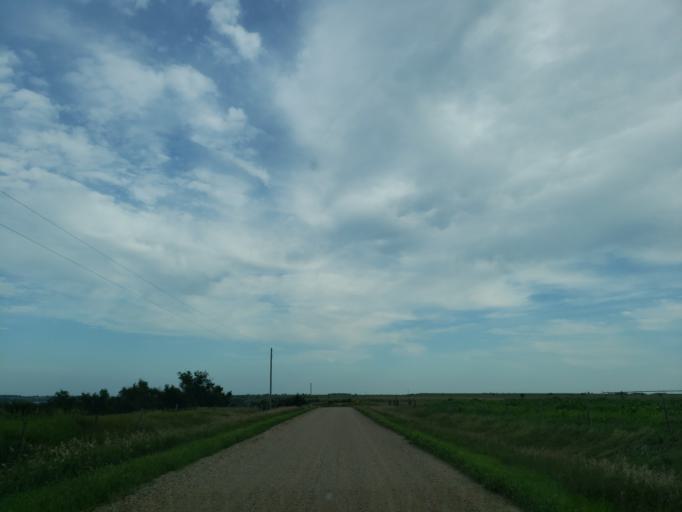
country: US
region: South Dakota
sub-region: Davison County
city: Mitchell
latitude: 43.6862
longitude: -97.9711
